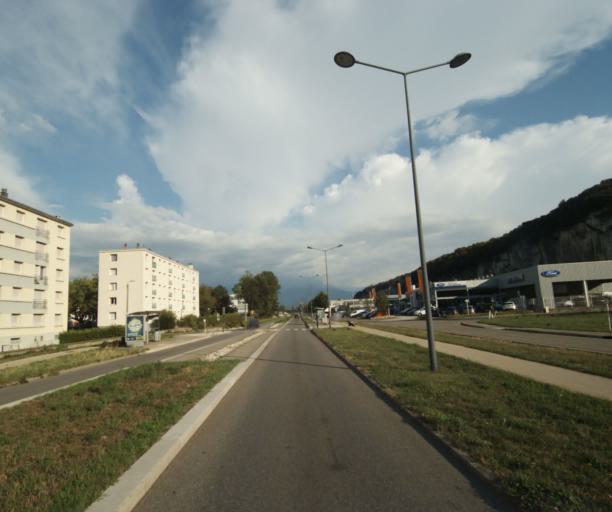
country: FR
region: Rhone-Alpes
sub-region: Departement de l'Isere
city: Fontaine
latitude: 45.1931
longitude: 5.6775
